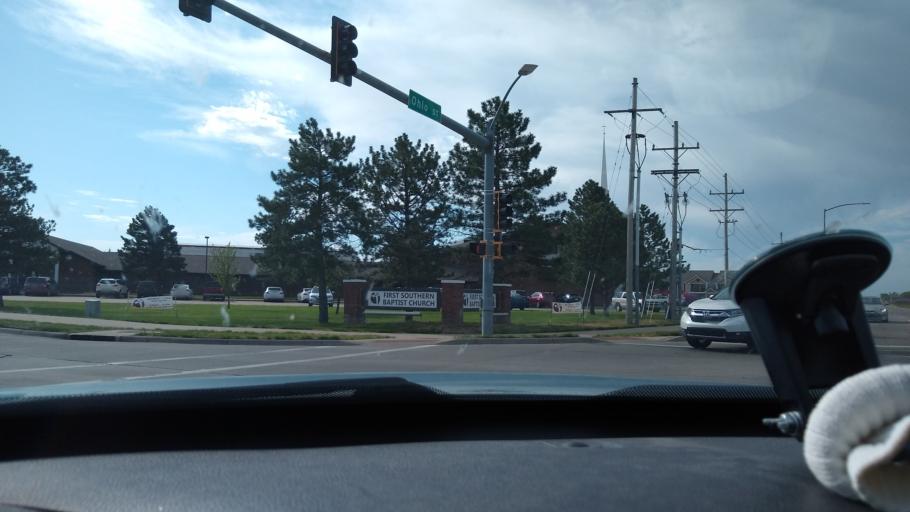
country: US
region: Kansas
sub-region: Saline County
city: Salina
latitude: 38.7980
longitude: -97.5942
